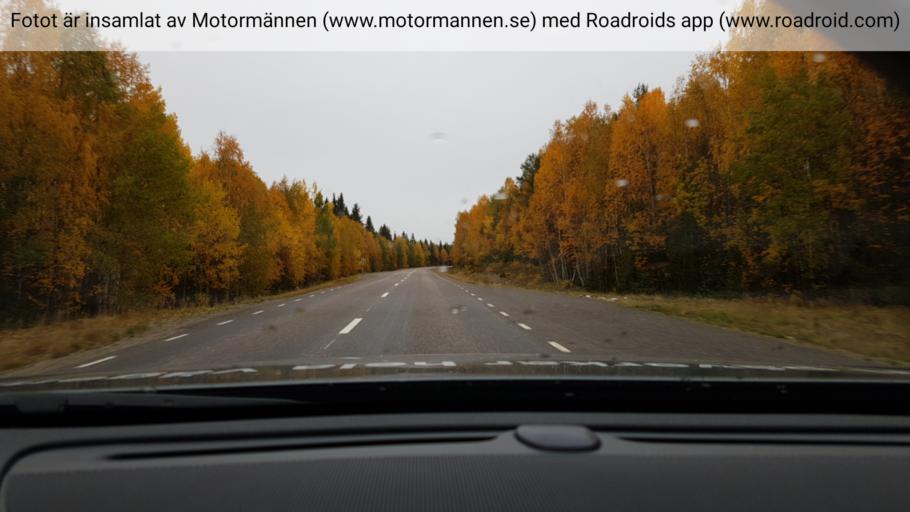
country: SE
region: Norrbotten
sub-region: Overkalix Kommun
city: OEverkalix
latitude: 66.5847
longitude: 22.7569
